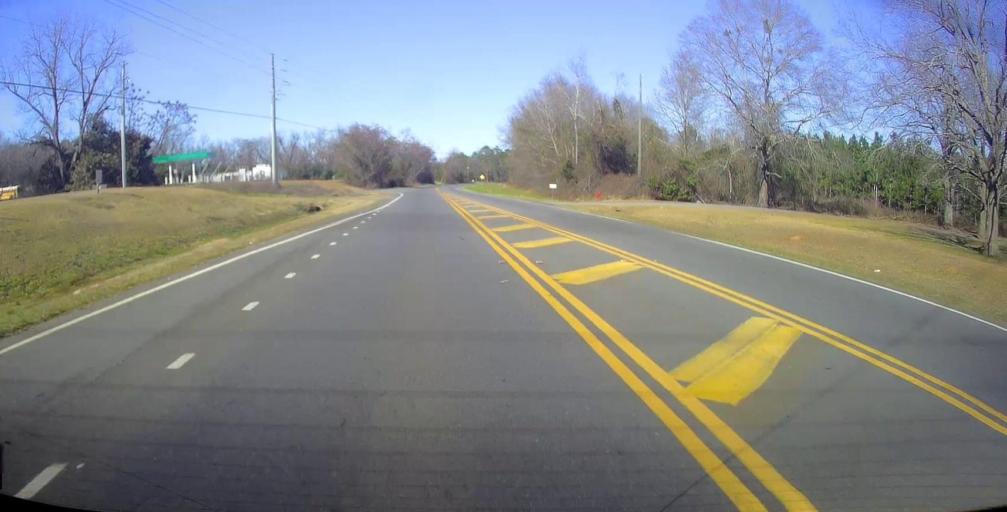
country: US
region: Georgia
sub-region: Macon County
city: Oglethorpe
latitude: 32.2617
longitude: -84.0857
